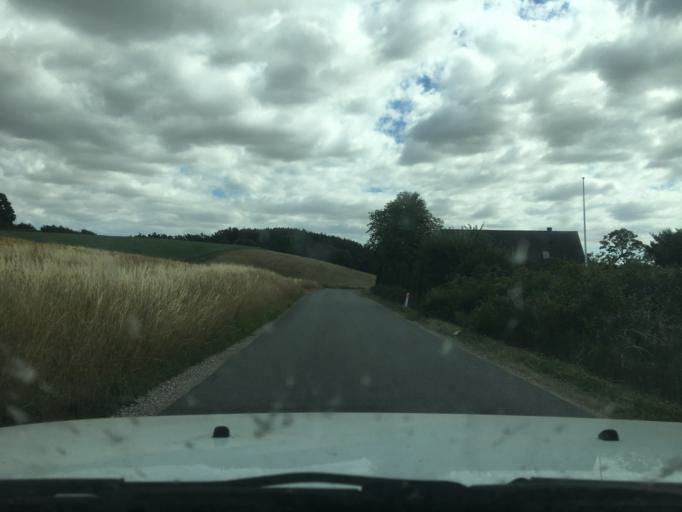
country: DK
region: Central Jutland
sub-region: Syddjurs Kommune
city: Ryomgard
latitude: 56.4543
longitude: 10.6362
